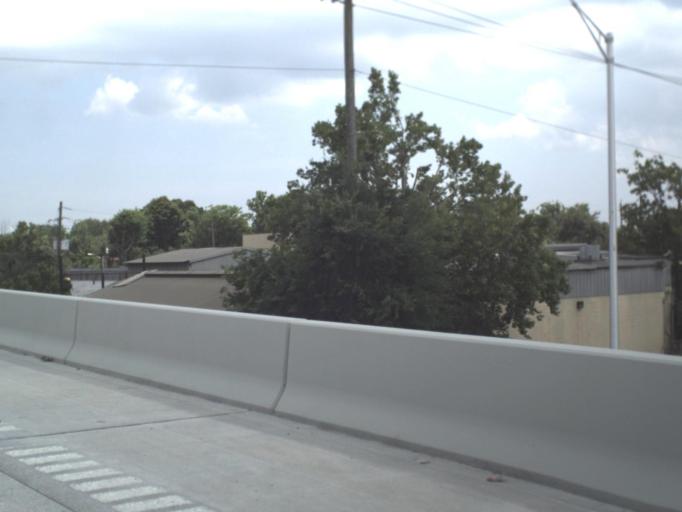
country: US
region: Florida
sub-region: Duval County
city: Jacksonville
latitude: 30.3562
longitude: -81.6422
